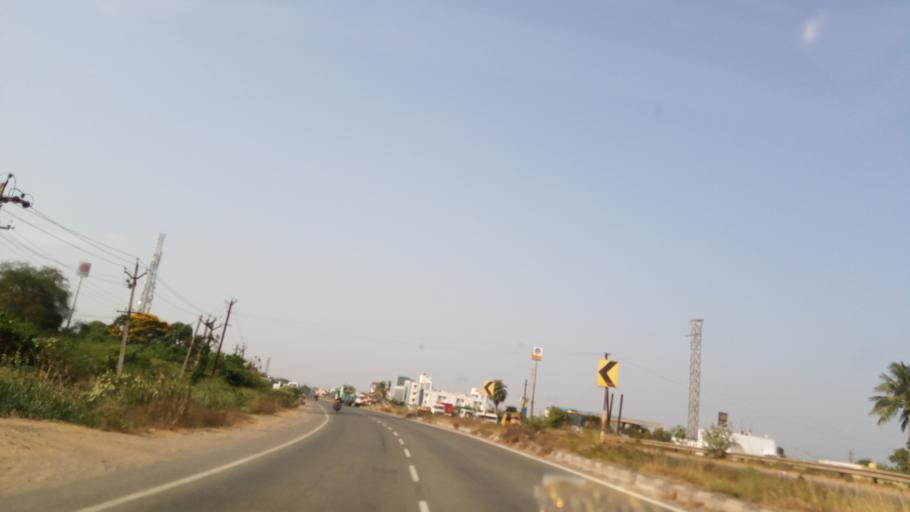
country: IN
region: Tamil Nadu
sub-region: Kancheepuram
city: Sriperumbudur
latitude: 12.9660
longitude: 79.9530
